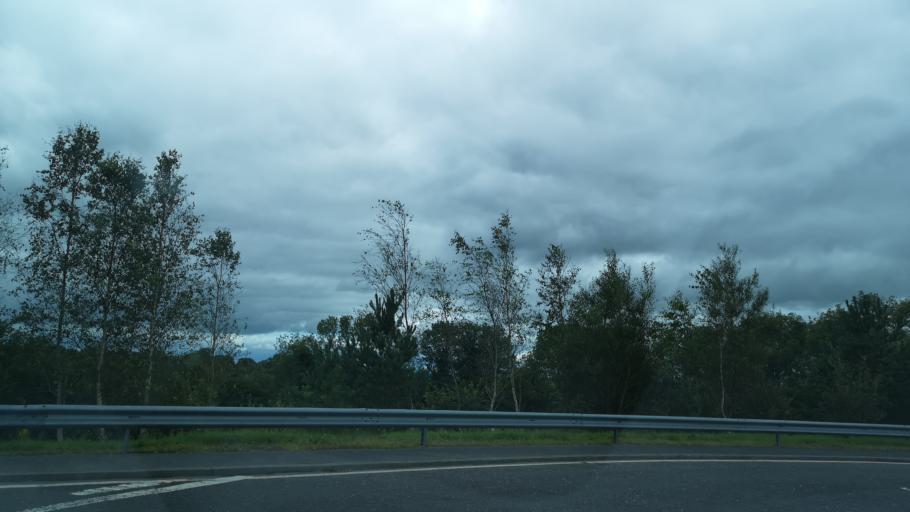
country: IE
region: Connaught
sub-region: County Galway
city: Ballinasloe
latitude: 53.3130
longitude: -8.1778
